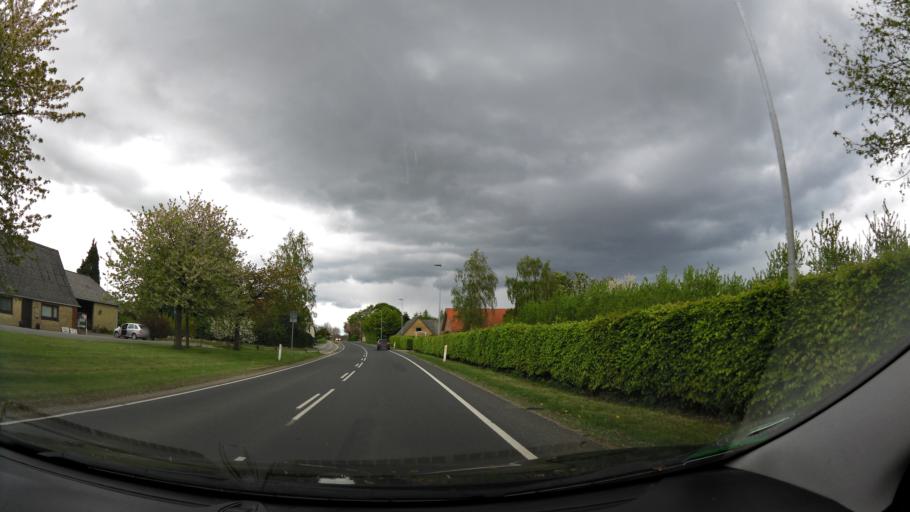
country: DK
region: South Denmark
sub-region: Nyborg Kommune
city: Nyborg
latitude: 55.2211
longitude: 10.7338
